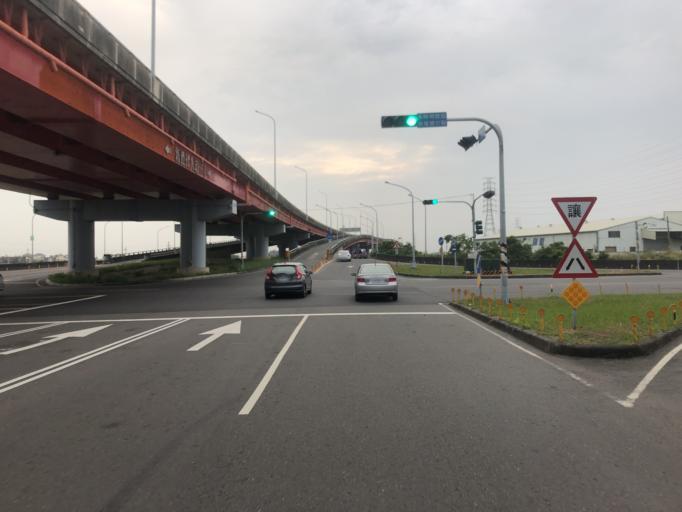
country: TW
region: Taiwan
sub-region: Tainan
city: Tainan
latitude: 23.0847
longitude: 120.2806
